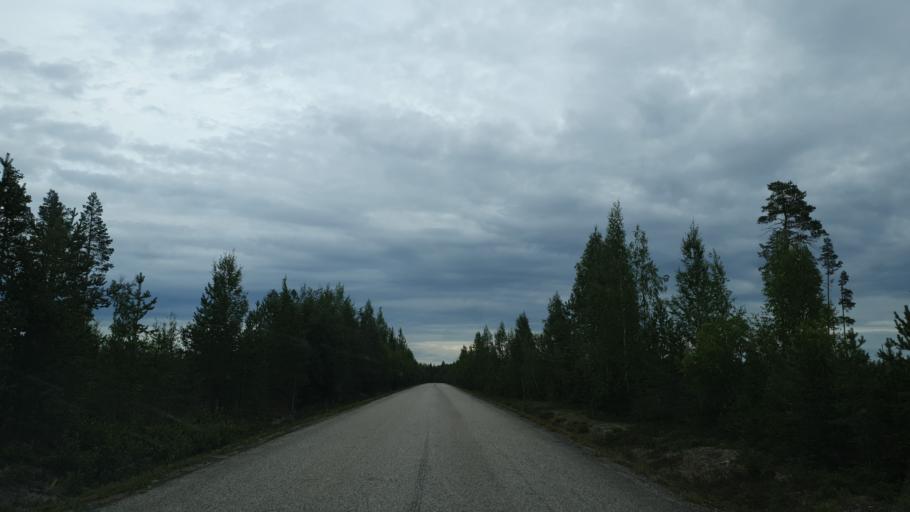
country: FI
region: Kainuu
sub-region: Kehys-Kainuu
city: Kuhmo
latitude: 64.3508
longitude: 29.1251
